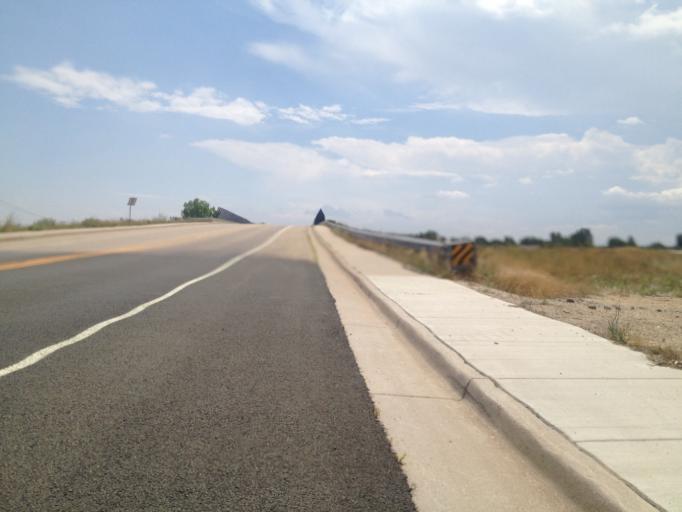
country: US
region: Colorado
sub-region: Boulder County
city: Superior
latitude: 39.9471
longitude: -105.1471
